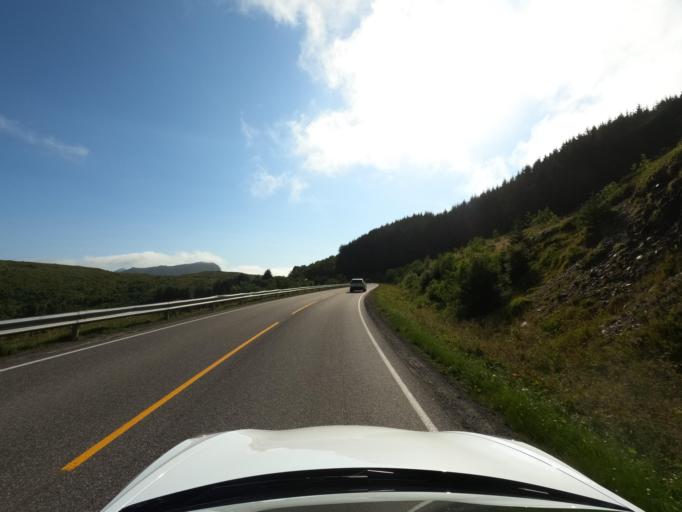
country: NO
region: Nordland
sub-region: Vestvagoy
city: Evjen
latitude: 68.2668
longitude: 13.8342
